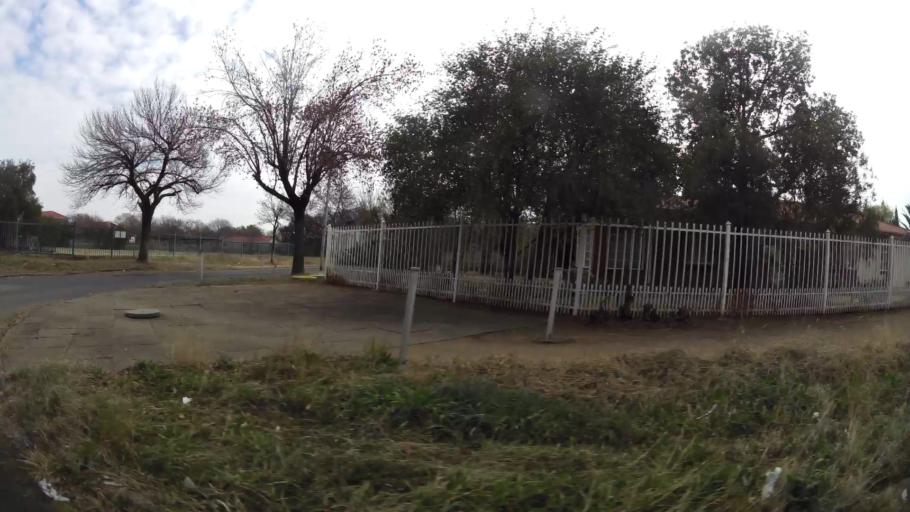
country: ZA
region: Orange Free State
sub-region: Mangaung Metropolitan Municipality
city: Bloemfontein
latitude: -29.1306
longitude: 26.1964
